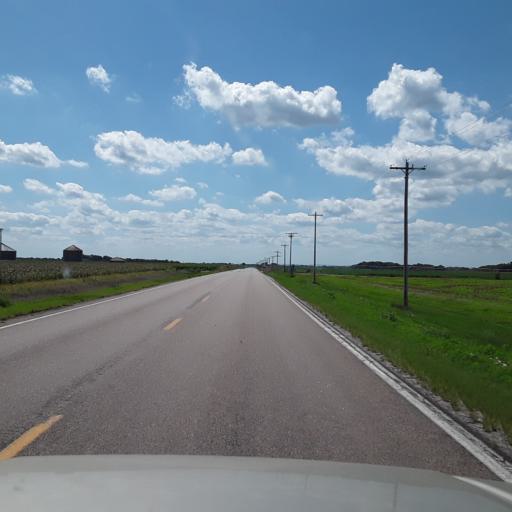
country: US
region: Nebraska
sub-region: Merrick County
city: Central City
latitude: 41.1911
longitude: -98.0372
